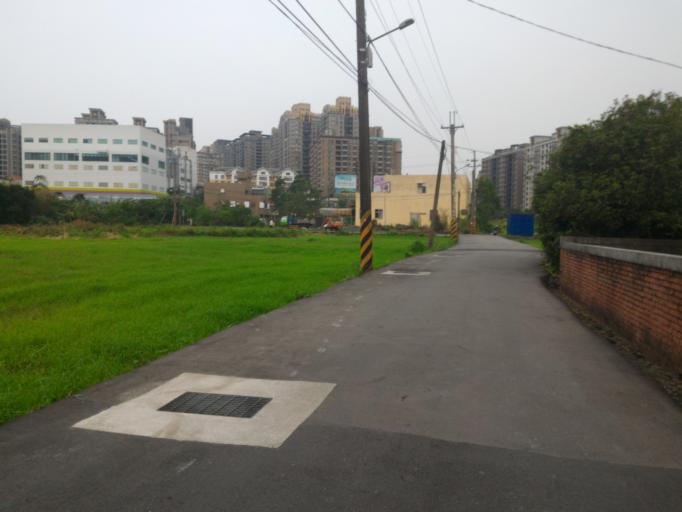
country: TW
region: Taiwan
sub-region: Taoyuan
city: Taoyuan
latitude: 24.9477
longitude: 121.3878
